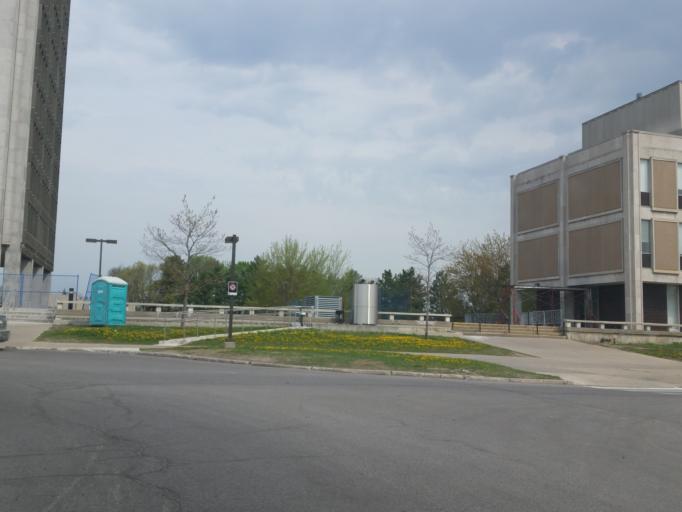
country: CA
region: Ontario
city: Ottawa
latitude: 45.4083
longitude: -75.7366
